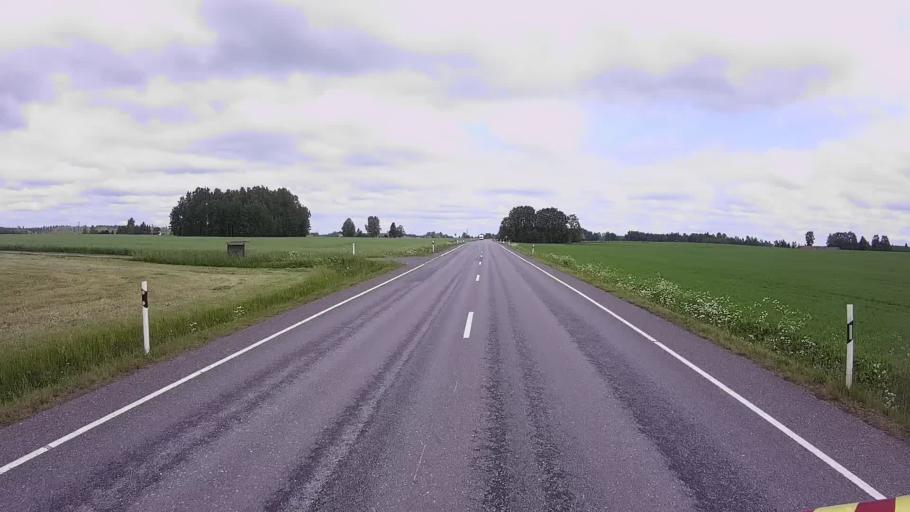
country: EE
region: Polvamaa
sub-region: Polva linn
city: Polva
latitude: 57.9483
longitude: 27.0499
